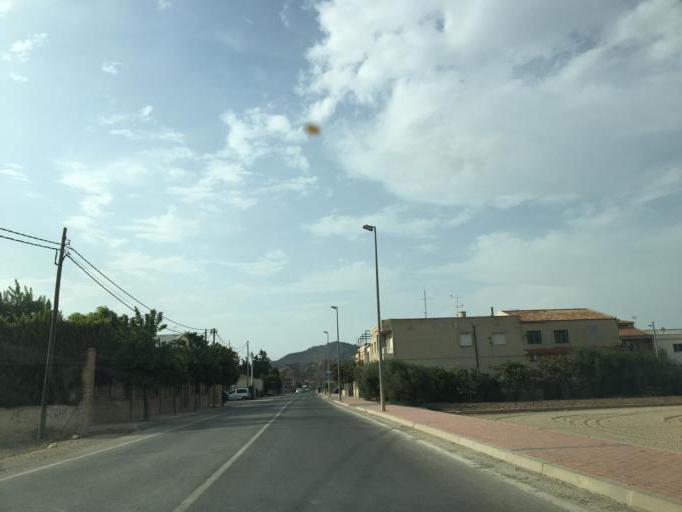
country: ES
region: Murcia
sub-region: Murcia
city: Murcia
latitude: 38.0159
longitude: -1.0833
